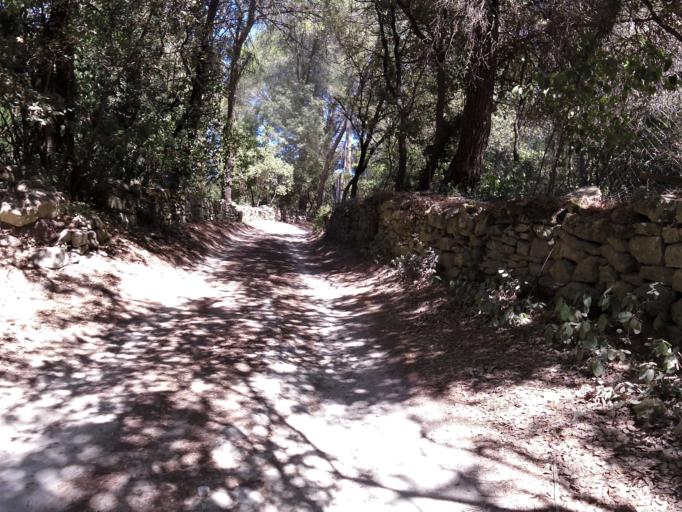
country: FR
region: Languedoc-Roussillon
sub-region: Departement du Gard
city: Aubais
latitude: 43.7463
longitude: 4.1485
